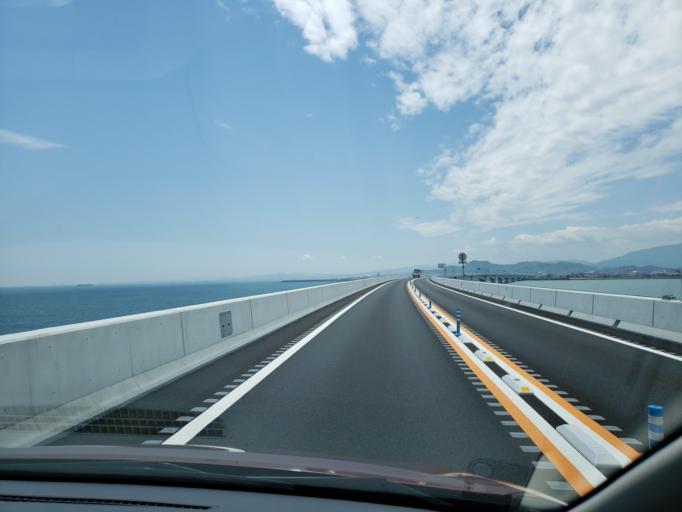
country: JP
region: Tokushima
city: Tokushima-shi
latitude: 34.0844
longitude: 134.6020
